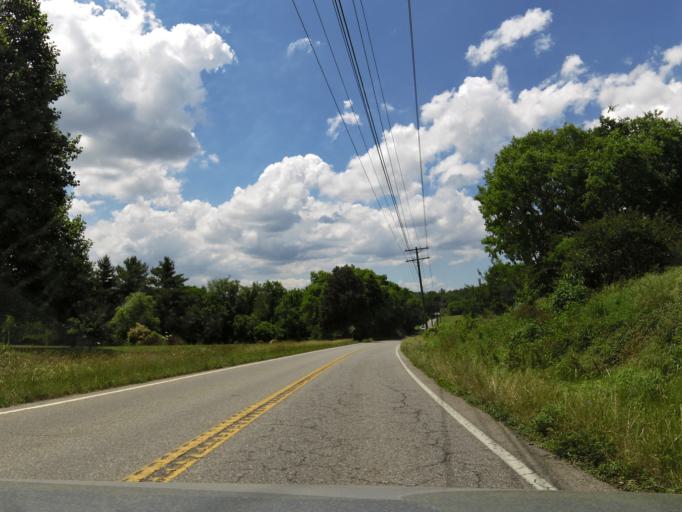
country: US
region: Tennessee
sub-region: Loudon County
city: Greenback
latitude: 35.6584
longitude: -84.0568
